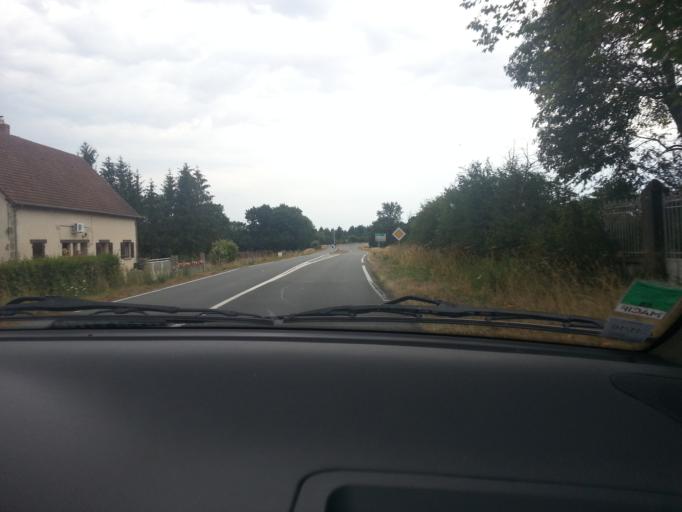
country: FR
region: Auvergne
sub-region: Departement de l'Allier
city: Saint-Gerand-le-Puy
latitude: 46.2048
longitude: 3.4996
